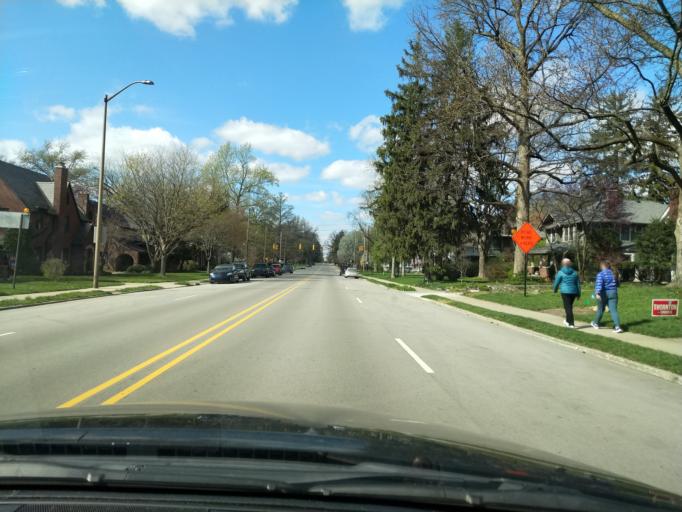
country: US
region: Indiana
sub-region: Marion County
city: Broad Ripple
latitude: 39.8500
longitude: -86.1501
